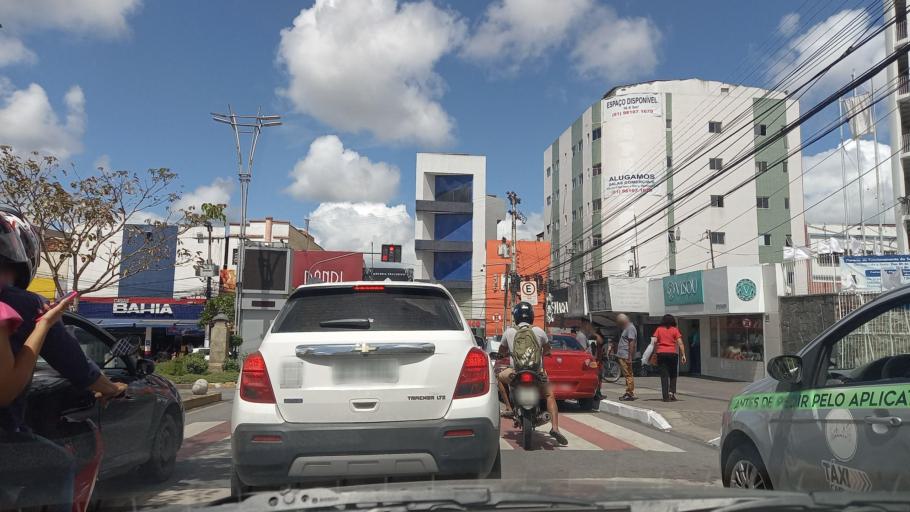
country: BR
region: Pernambuco
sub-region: Caruaru
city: Caruaru
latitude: -8.2852
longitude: -35.9706
